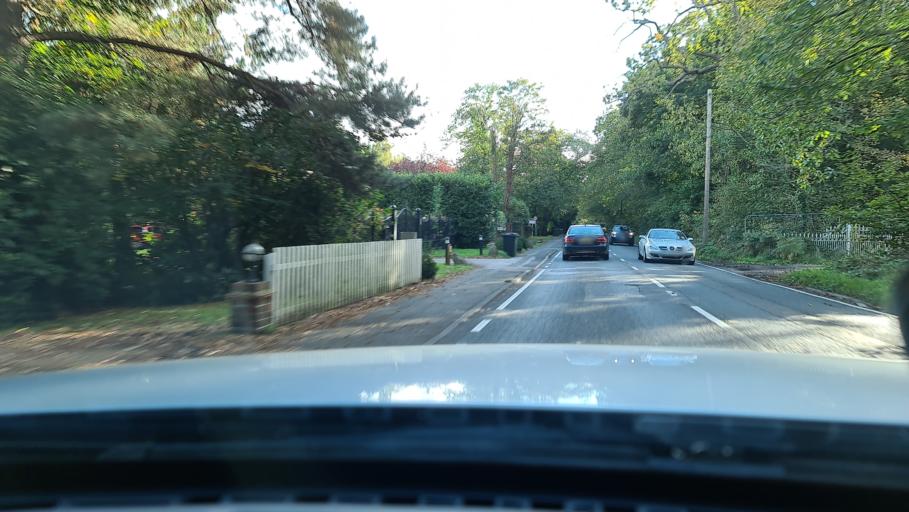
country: GB
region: England
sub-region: Surrey
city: Cobham
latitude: 51.3410
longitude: -0.4348
